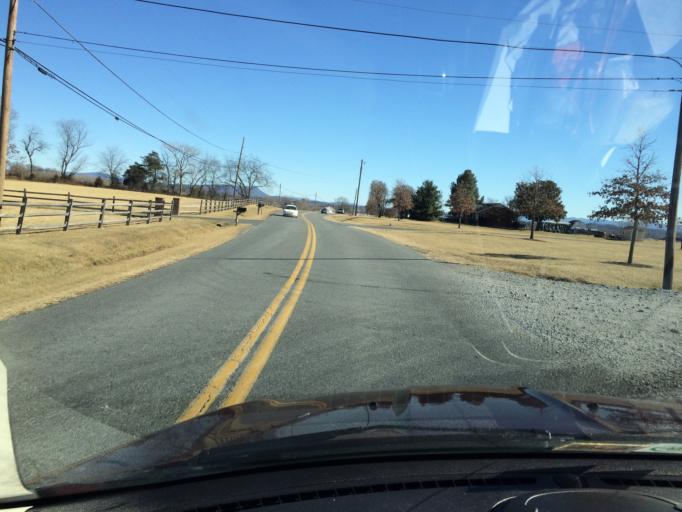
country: US
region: Virginia
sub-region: Rockingham County
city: Bridgewater
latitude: 38.3658
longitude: -78.9732
